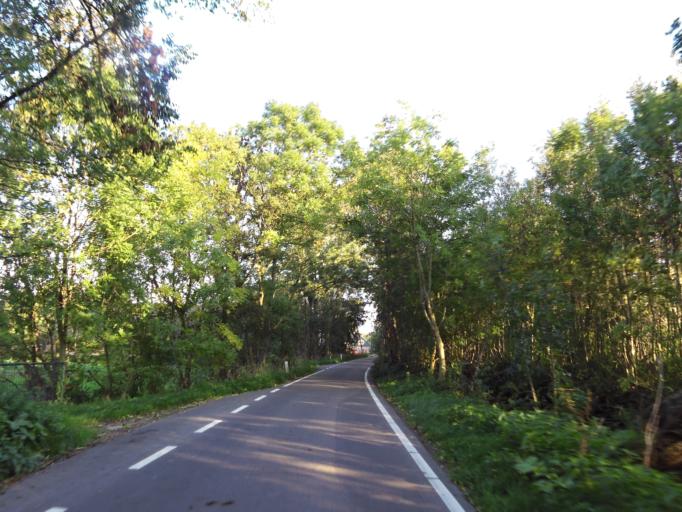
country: NL
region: South Holland
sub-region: Gemeente Alphen aan den Rijn
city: Alphen aan den Rijn
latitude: 52.1419
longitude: 4.6221
